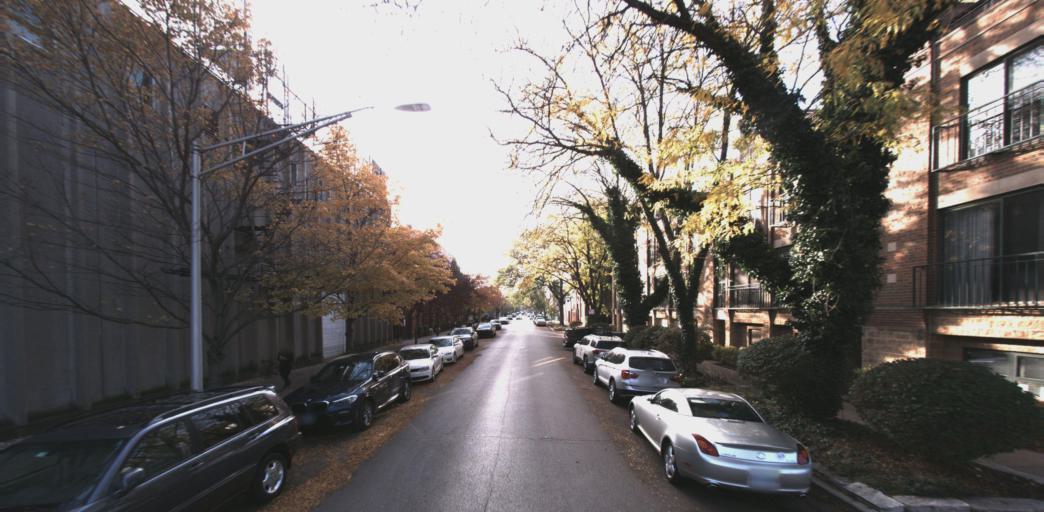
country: US
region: Illinois
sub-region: Cook County
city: Chicago
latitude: 41.9271
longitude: -87.6615
